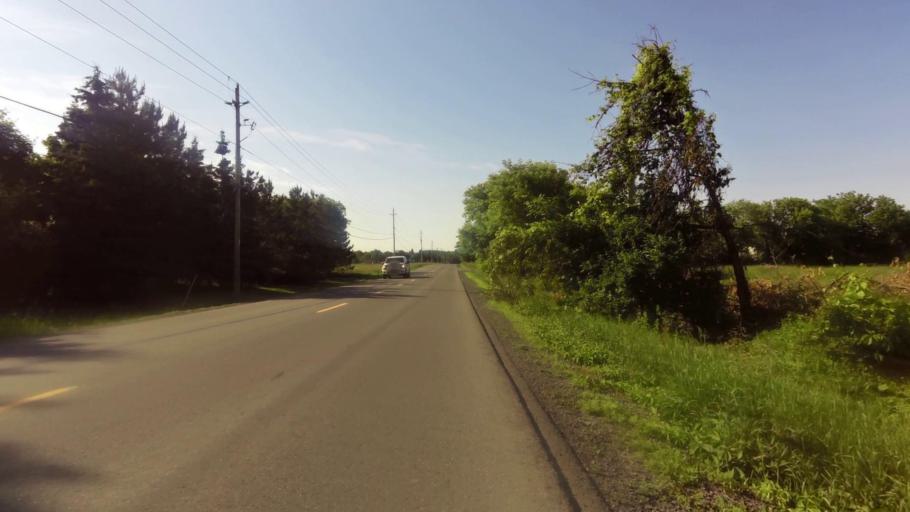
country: CA
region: Ontario
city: Ottawa
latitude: 45.2495
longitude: -75.5632
